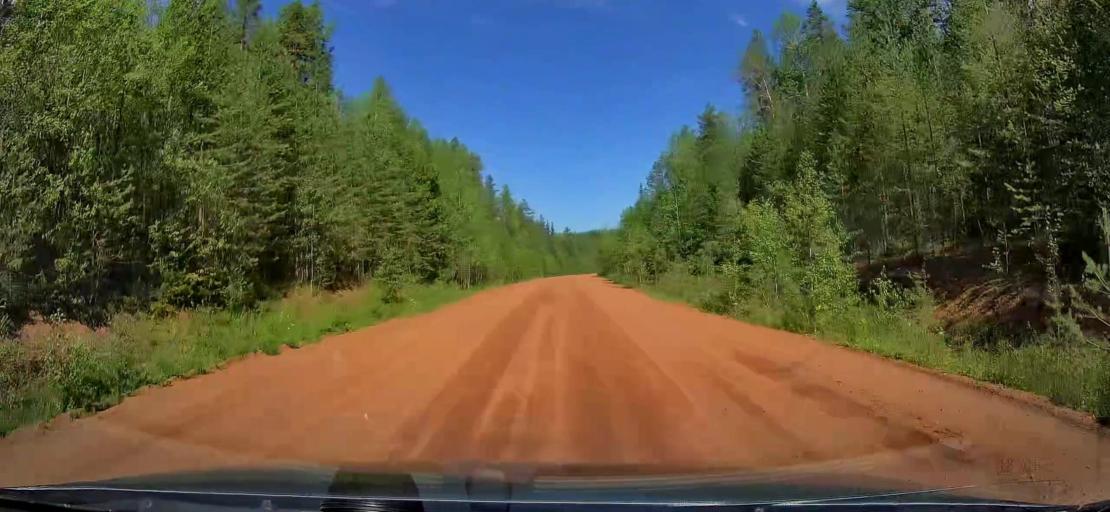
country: RU
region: Arkhangelskaya
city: Leshukonskoye
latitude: 65.3448
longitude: 45.1289
